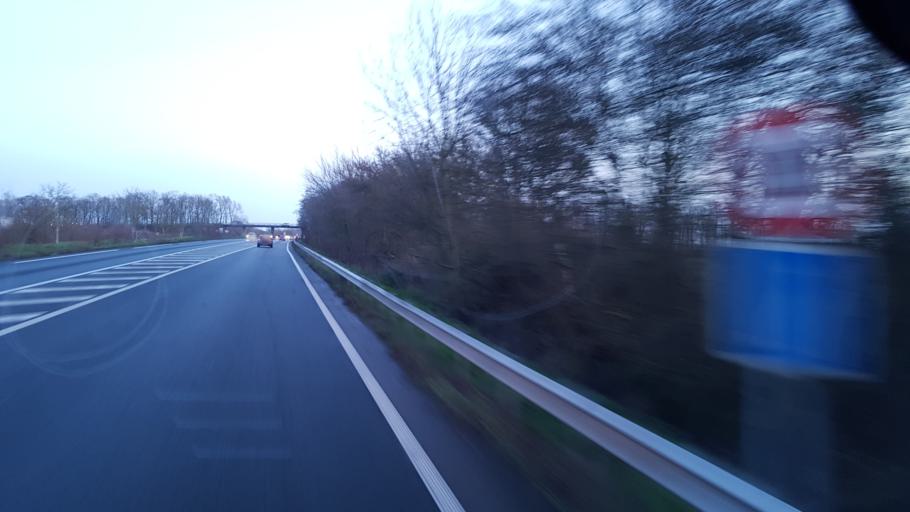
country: FR
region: Nord-Pas-de-Calais
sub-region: Departement du Nord
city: Lambres-lez-Douai
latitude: 50.3442
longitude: 3.0750
